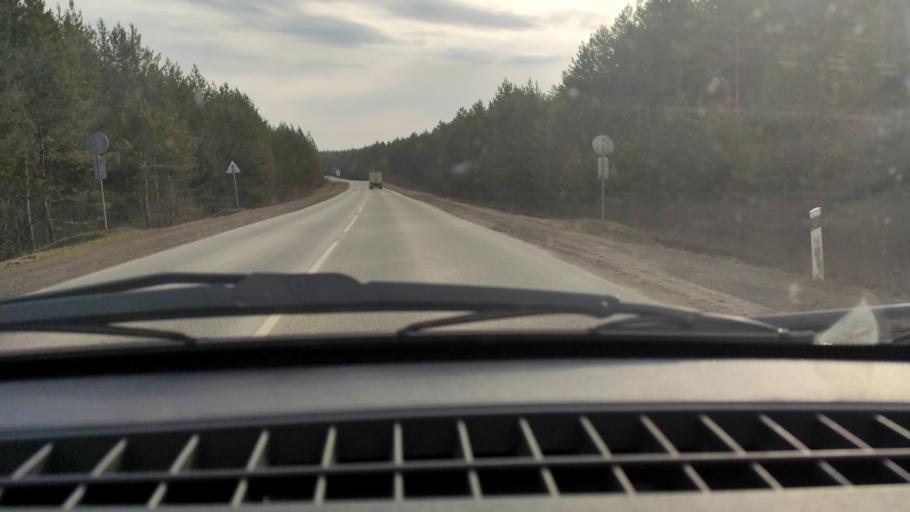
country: RU
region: Bashkortostan
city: Davlekanovo
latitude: 54.2414
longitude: 55.0652
